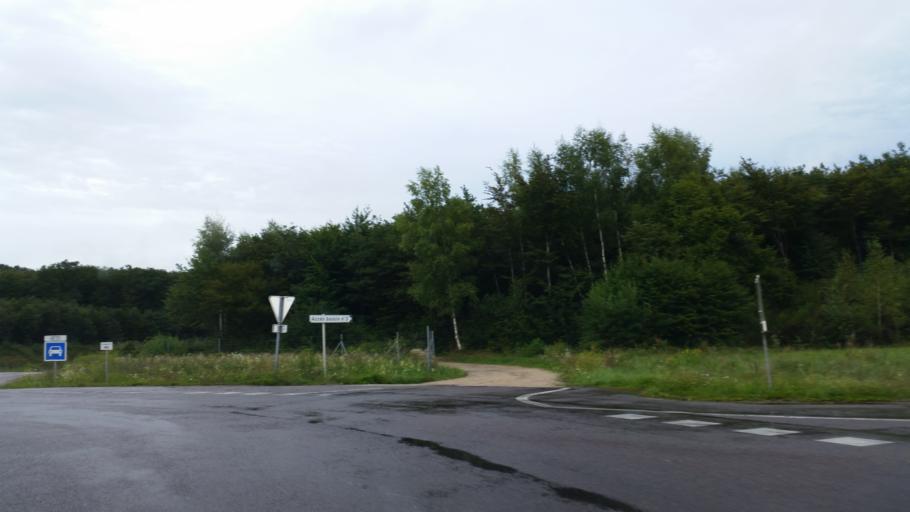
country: FR
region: Franche-Comte
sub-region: Departement de la Haute-Saone
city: Magny-Vernois
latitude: 47.6952
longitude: 6.4692
